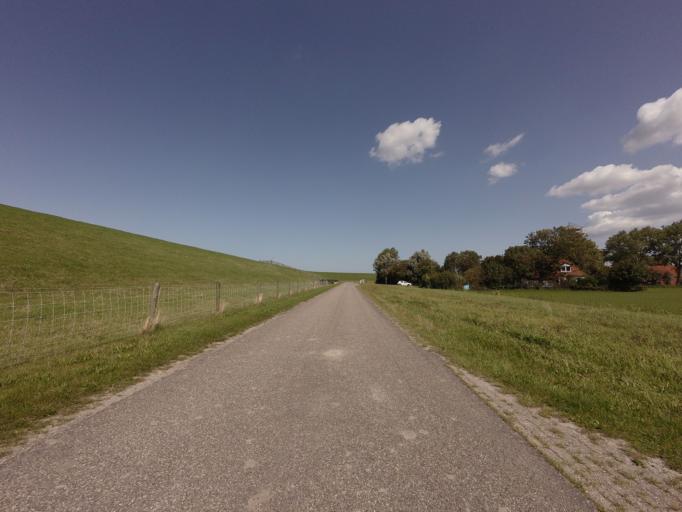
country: NL
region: Friesland
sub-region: Gemeente Ferwerderadiel
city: Hallum
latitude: 53.3278
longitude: 5.7708
